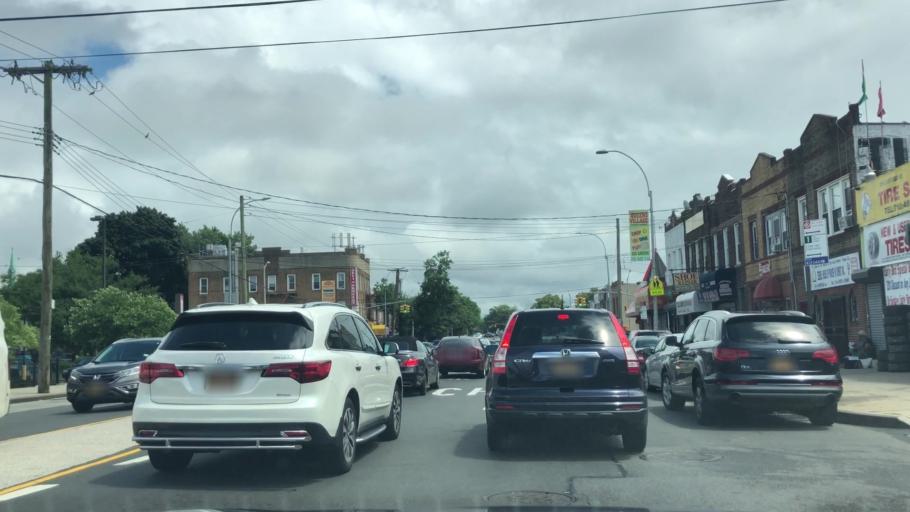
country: US
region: New York
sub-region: Nassau County
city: Bellerose Terrace
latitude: 40.7135
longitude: -73.7367
